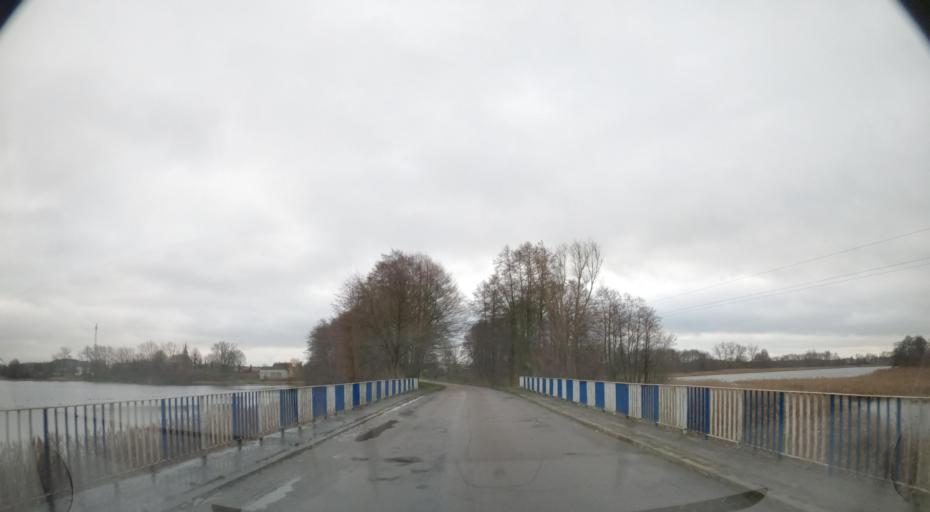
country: PL
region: Greater Poland Voivodeship
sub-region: Powiat pilski
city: Wysoka
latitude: 53.2577
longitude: 17.1174
